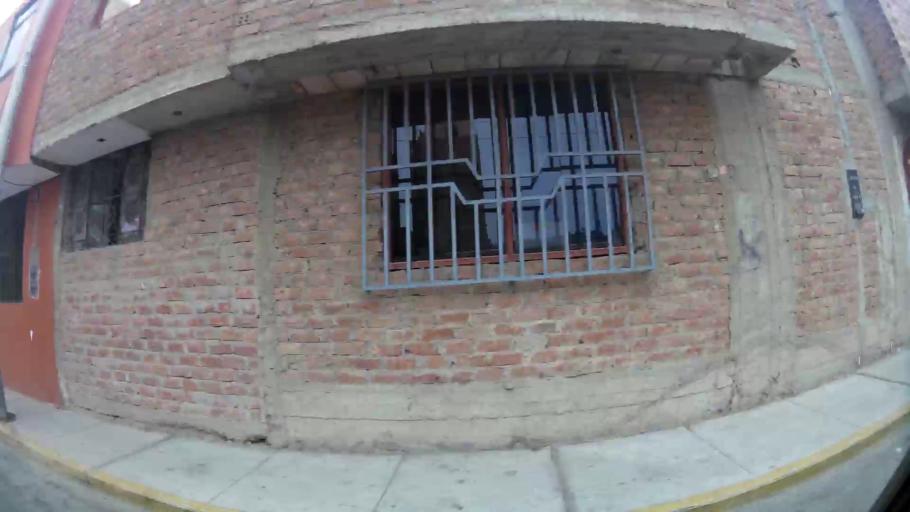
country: PE
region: La Libertad
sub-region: Provincia de Trujillo
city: Trujillo
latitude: -8.1249
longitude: -79.0264
